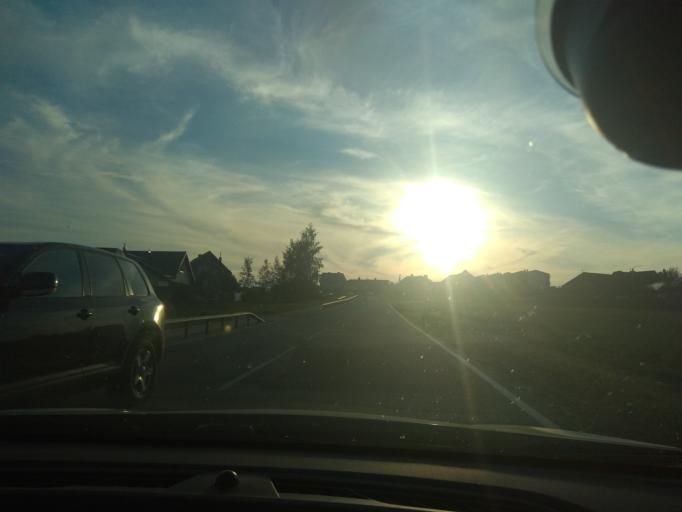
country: LT
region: Klaipedos apskritis
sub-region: Klaipeda
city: Klaipeda
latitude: 55.7531
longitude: 21.1678
